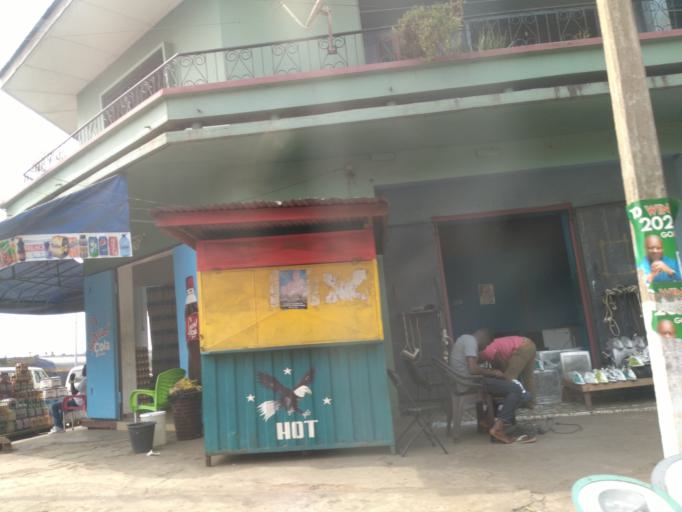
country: GH
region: Ashanti
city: Kumasi
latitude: 6.7022
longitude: -1.6175
